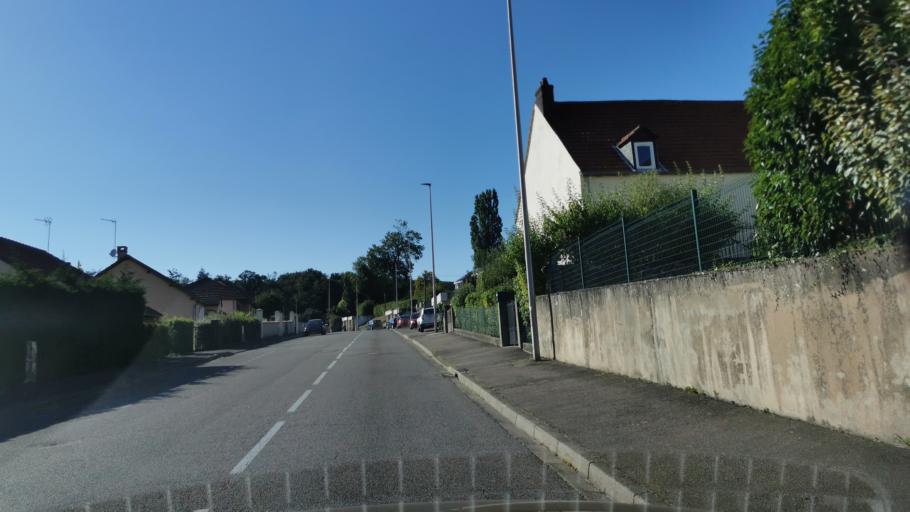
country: FR
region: Bourgogne
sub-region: Departement de Saone-et-Loire
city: Le Creusot
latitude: 46.8000
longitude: 4.4149
